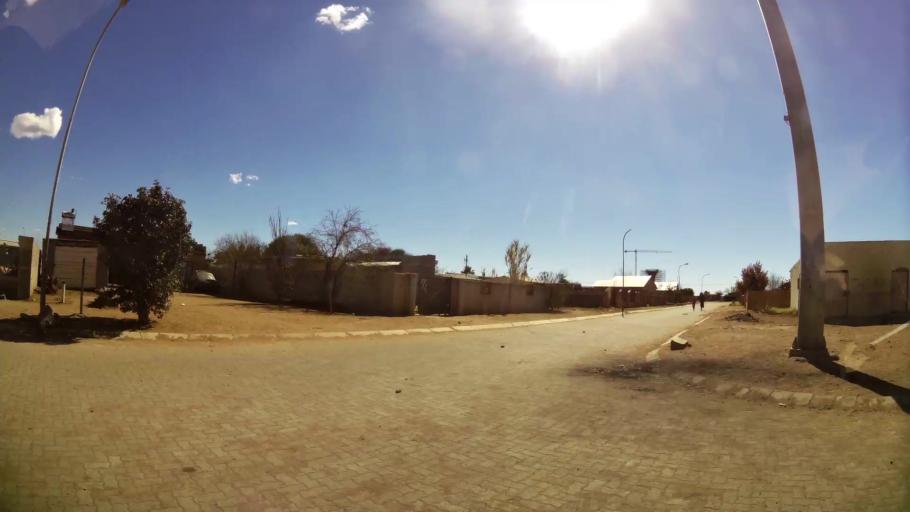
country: ZA
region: North-West
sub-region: Dr Kenneth Kaunda District Municipality
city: Klerksdorp
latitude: -26.8679
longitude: 26.5774
